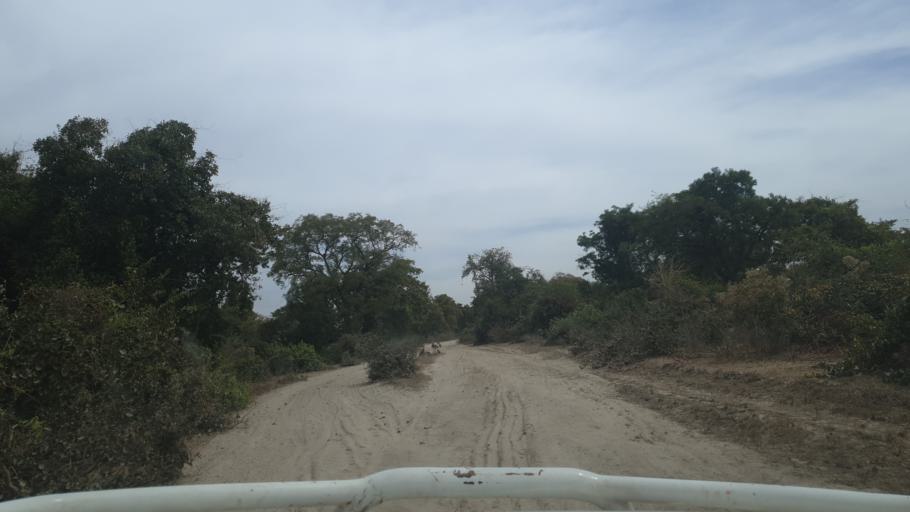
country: ML
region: Sikasso
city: Yorosso
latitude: 12.2374
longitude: -4.7398
